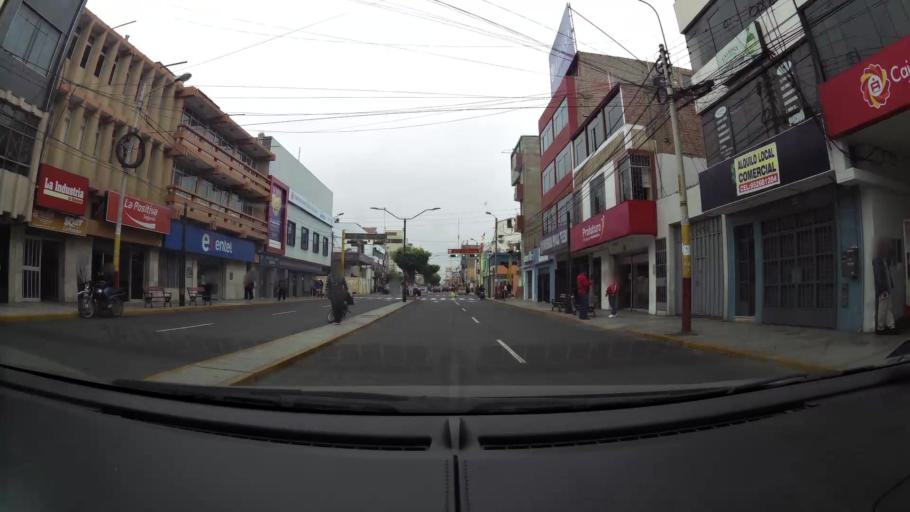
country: PE
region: Ancash
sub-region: Provincia de Santa
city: Chimbote
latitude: -9.0764
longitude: -78.5942
